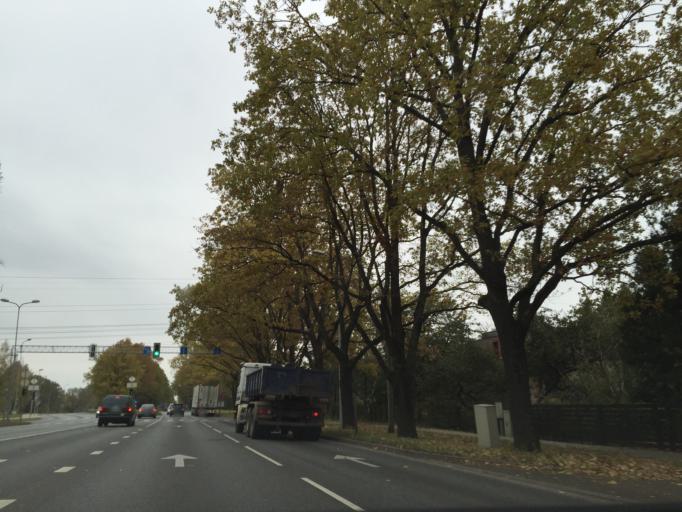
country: LV
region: Marupe
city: Marupe
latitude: 56.8998
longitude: 24.0787
